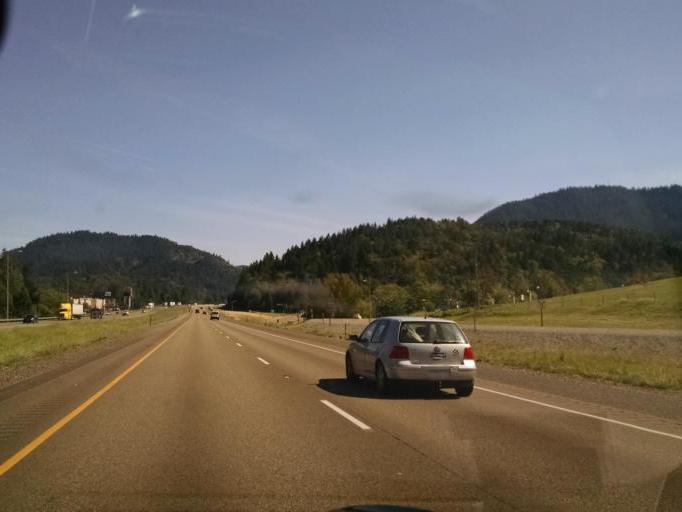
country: US
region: Oregon
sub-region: Douglas County
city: Canyonville
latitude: 42.9448
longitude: -123.2927
